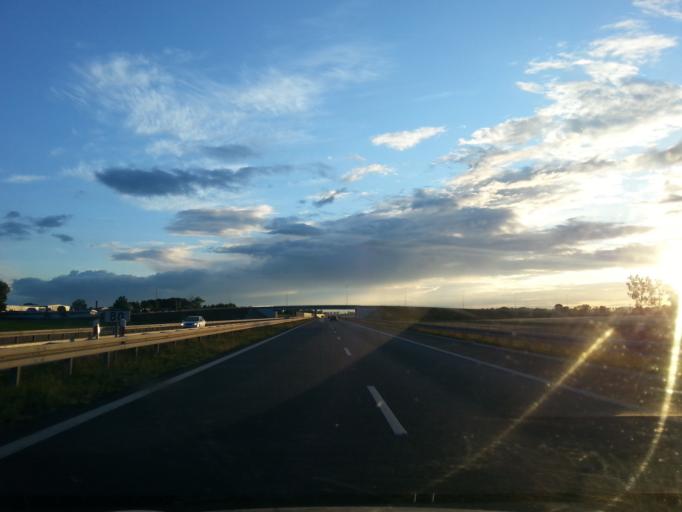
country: PL
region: Lower Silesian Voivodeship
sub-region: Powiat olesnicki
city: Sycow
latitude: 51.2937
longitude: 17.7190
